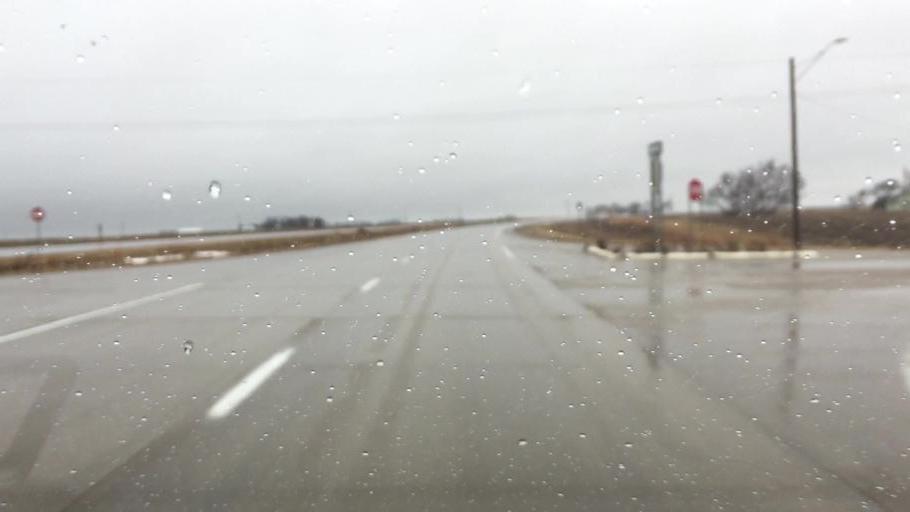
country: US
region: Iowa
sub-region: O'Brien County
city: Sheldon
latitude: 43.0693
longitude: -95.8969
